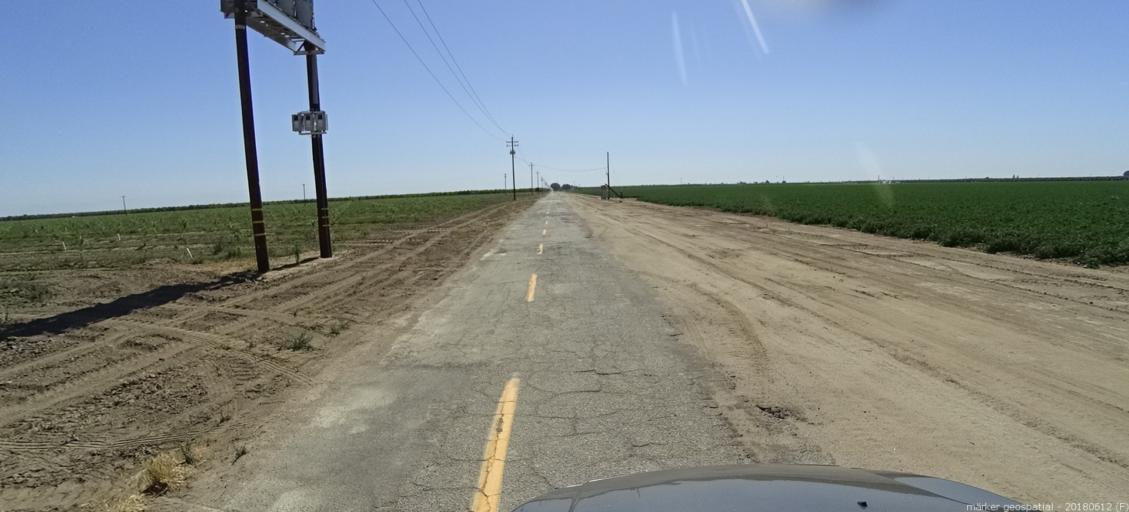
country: US
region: California
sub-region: Madera County
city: Chowchilla
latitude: 37.0325
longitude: -120.3809
